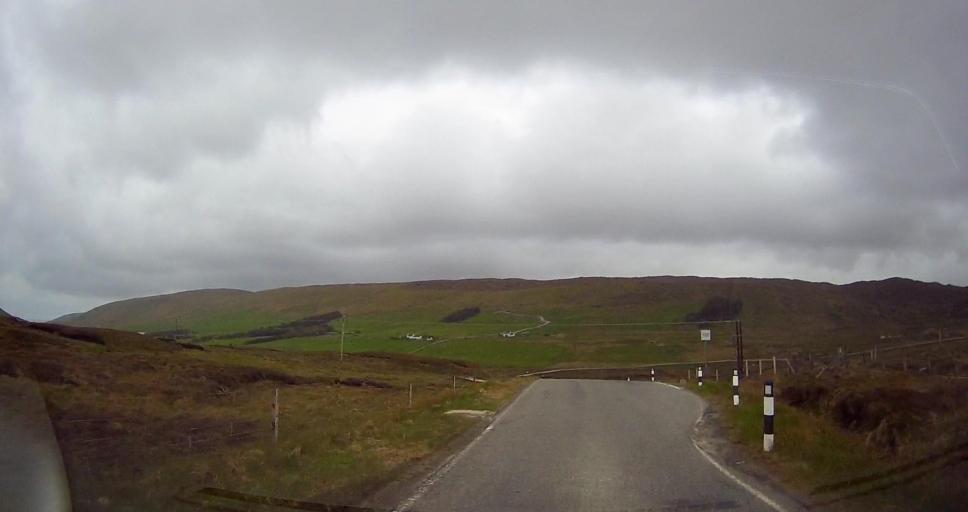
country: GB
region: Scotland
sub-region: Shetland Islands
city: Lerwick
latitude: 60.2783
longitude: -1.2687
